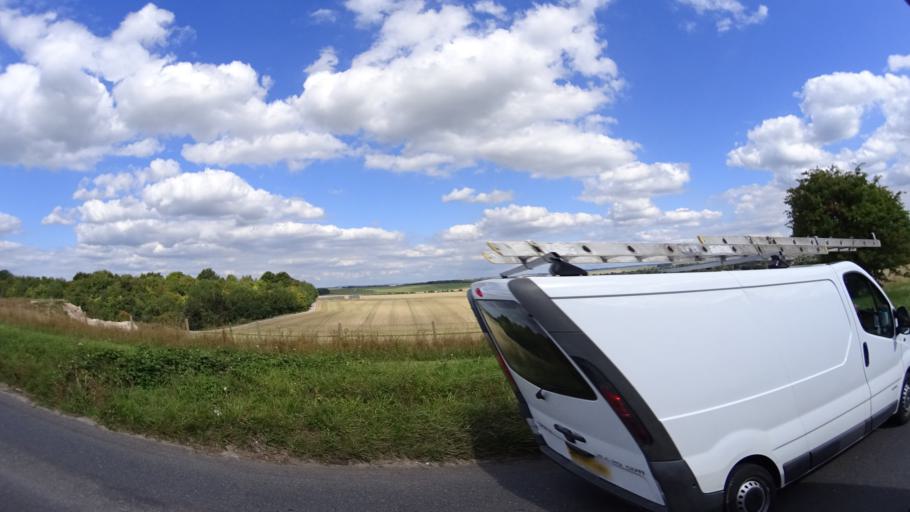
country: GB
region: England
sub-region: Wiltshire
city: Durrington
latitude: 51.1955
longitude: -1.7890
